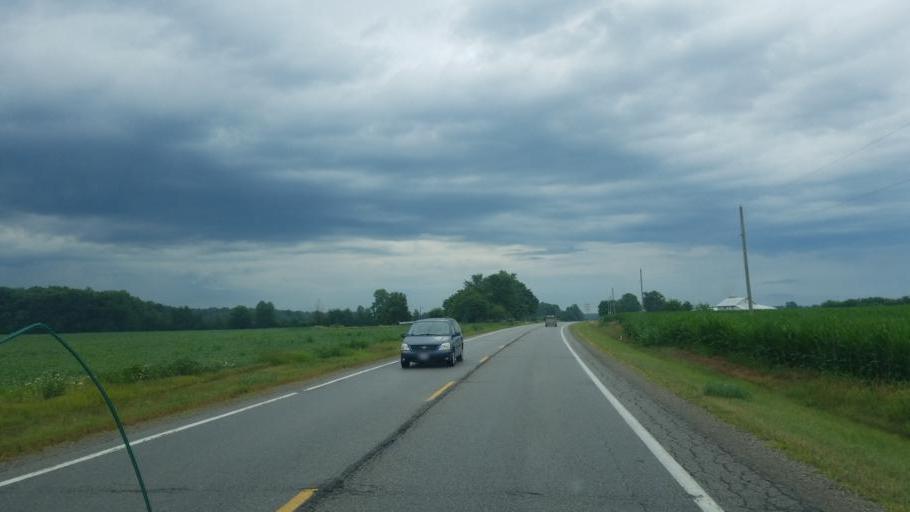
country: US
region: Ohio
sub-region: Williams County
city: Edgerton
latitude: 41.4469
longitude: -84.6826
